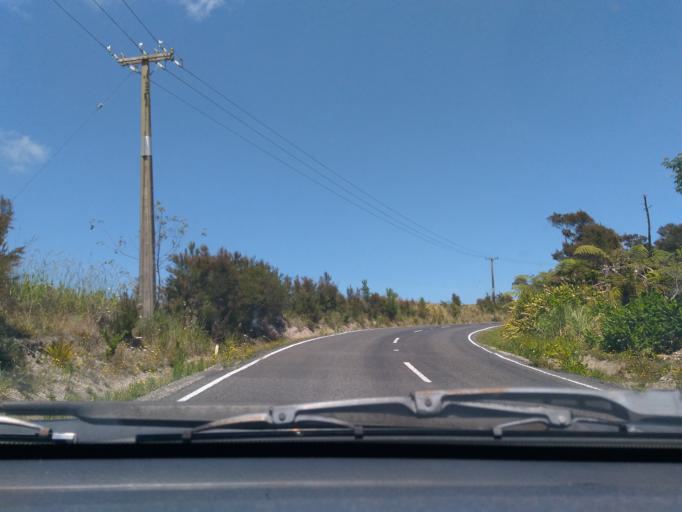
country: NZ
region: Northland
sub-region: Far North District
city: Taipa
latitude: -34.9946
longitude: 173.5254
